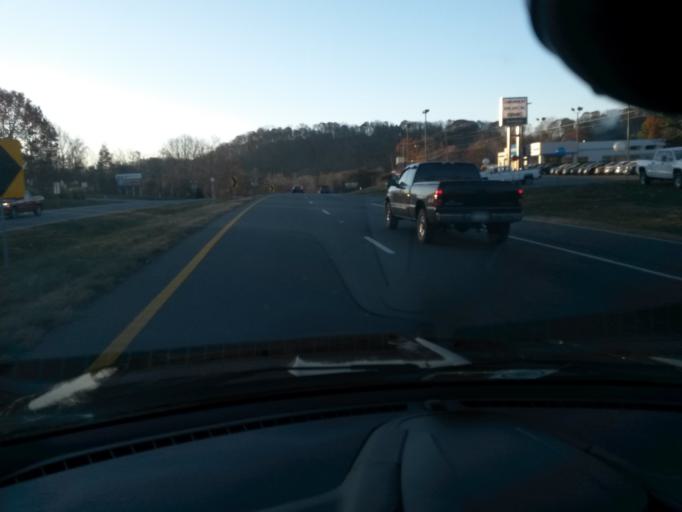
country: US
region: Virginia
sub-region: Franklin County
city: Rocky Mount
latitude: 37.0425
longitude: -79.8757
